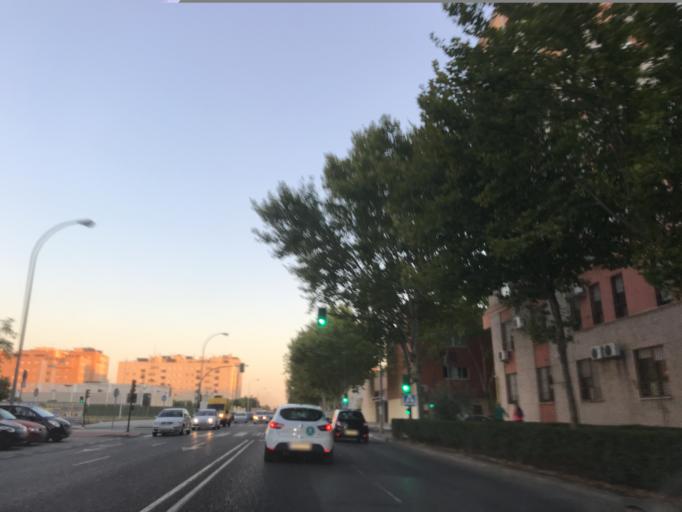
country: ES
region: Andalusia
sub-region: Provincia de Sevilla
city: Sevilla
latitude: 37.4017
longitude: -5.9206
